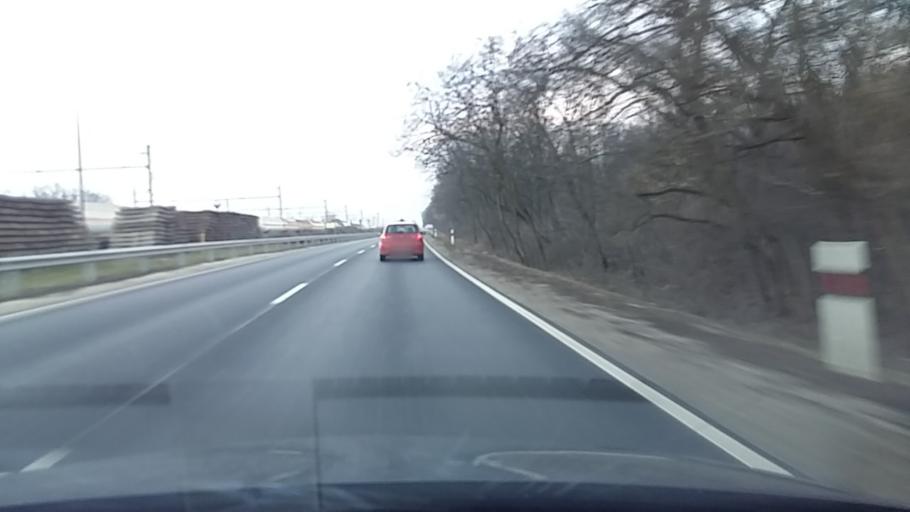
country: HU
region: Hajdu-Bihar
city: Debrecen
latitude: 47.5827
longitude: 21.6550
